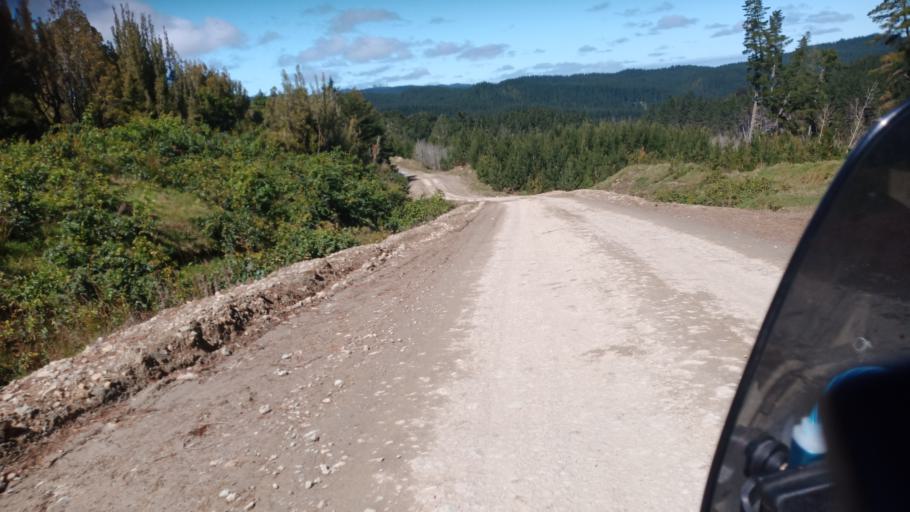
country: NZ
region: Gisborne
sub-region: Gisborne District
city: Gisborne
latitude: -38.8861
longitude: 177.7851
